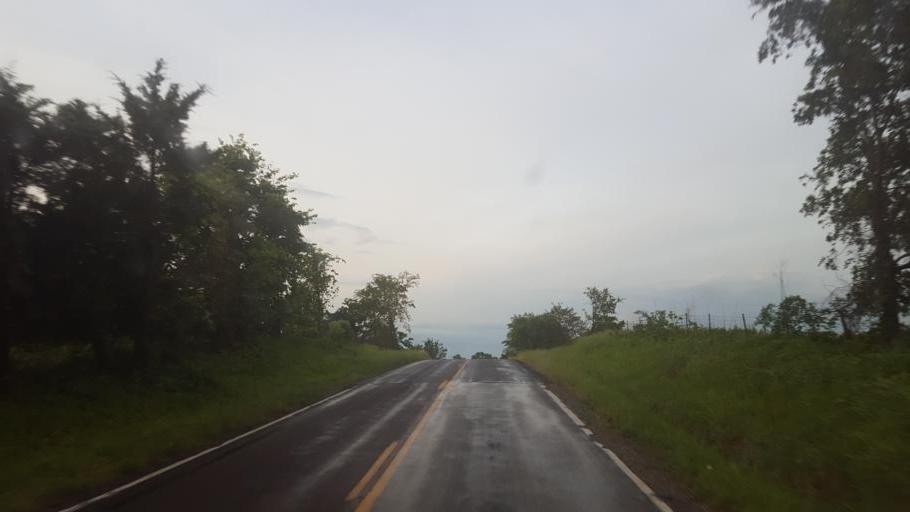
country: US
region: Missouri
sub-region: Moniteau County
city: California
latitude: 38.7031
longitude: -92.6349
